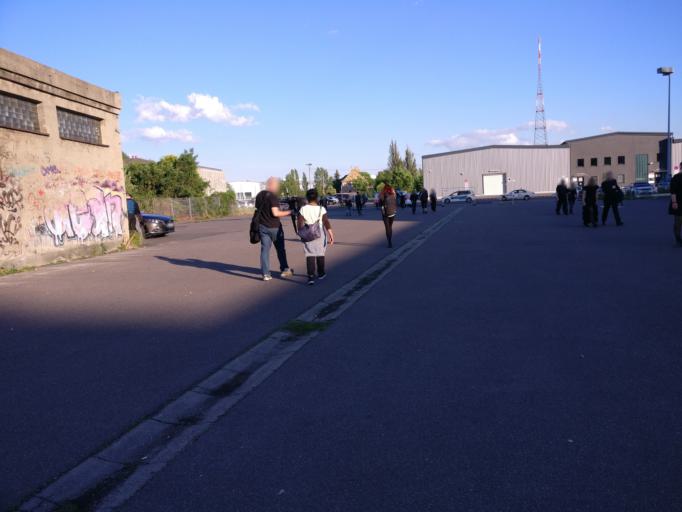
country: DE
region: Saxony
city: Leipzig
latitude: 51.3201
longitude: 12.3902
